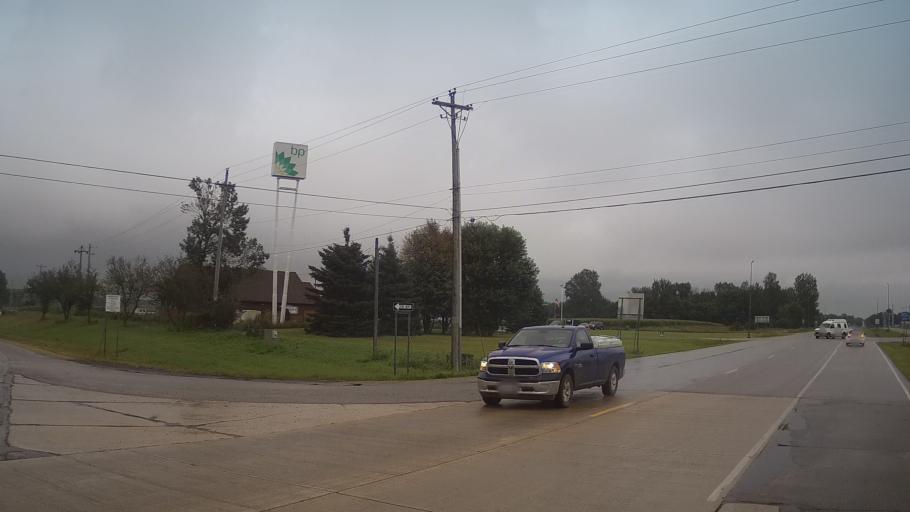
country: US
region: Minnesota
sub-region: Mower County
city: Austin
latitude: 43.6664
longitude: -93.0187
